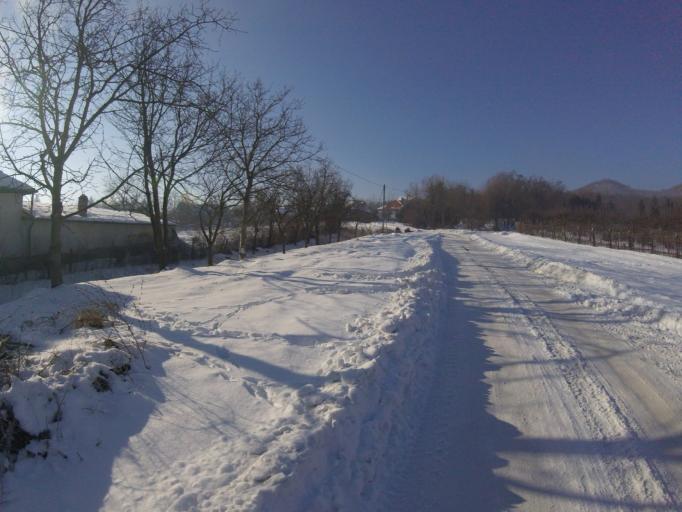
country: HU
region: Nograd
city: Diosjeno
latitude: 47.9463
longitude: 19.0285
